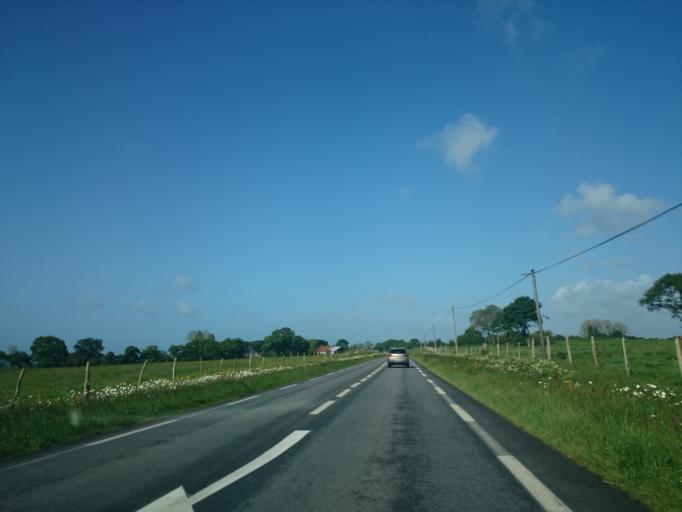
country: FR
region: Brittany
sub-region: Departement du Morbihan
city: Arradon
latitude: 47.6377
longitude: -2.8326
